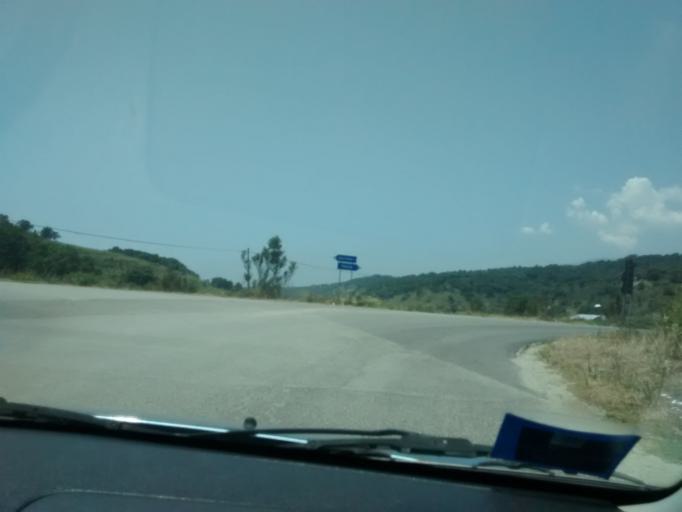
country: IT
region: Calabria
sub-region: Provincia di Catanzaro
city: Maida
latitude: 38.9006
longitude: 16.3867
